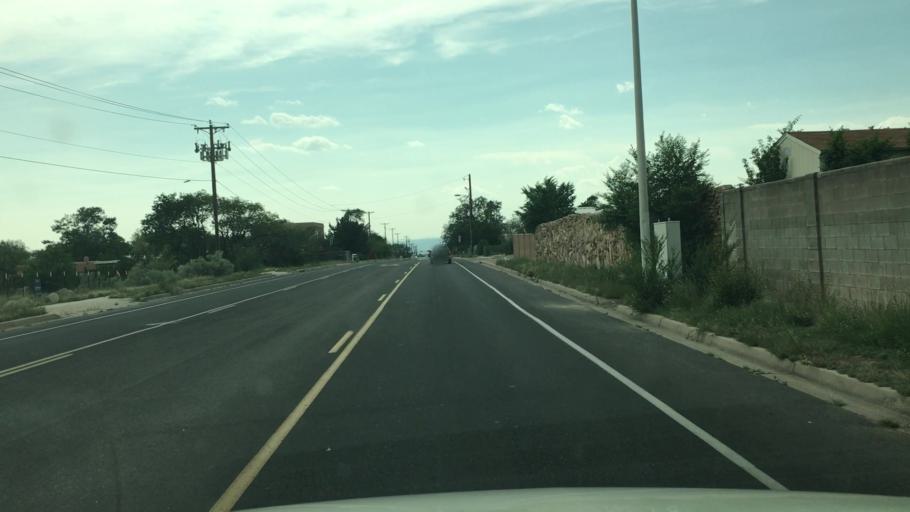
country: US
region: New Mexico
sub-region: Santa Fe County
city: Santa Fe
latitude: 35.6521
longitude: -105.9604
